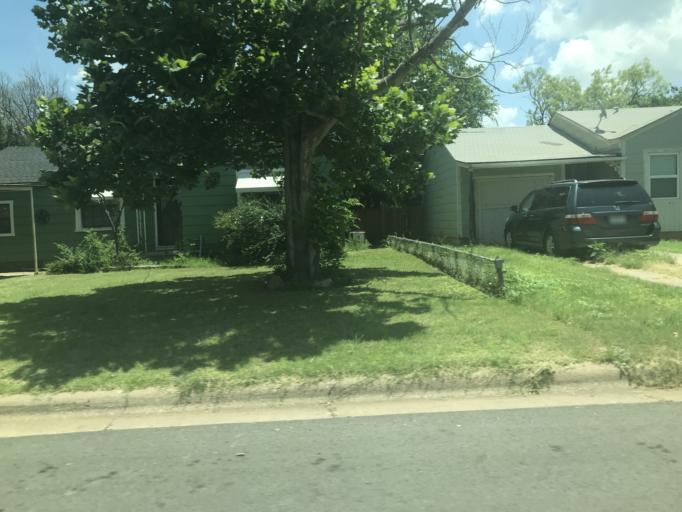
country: US
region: Texas
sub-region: Taylor County
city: Abilene
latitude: 32.4681
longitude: -99.7556
